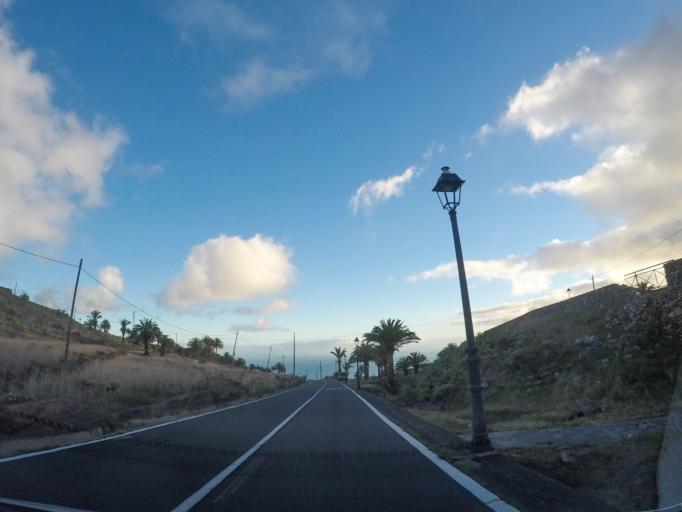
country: ES
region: Canary Islands
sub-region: Provincia de Santa Cruz de Tenerife
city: Alajero
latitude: 28.0688
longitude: -17.2388
